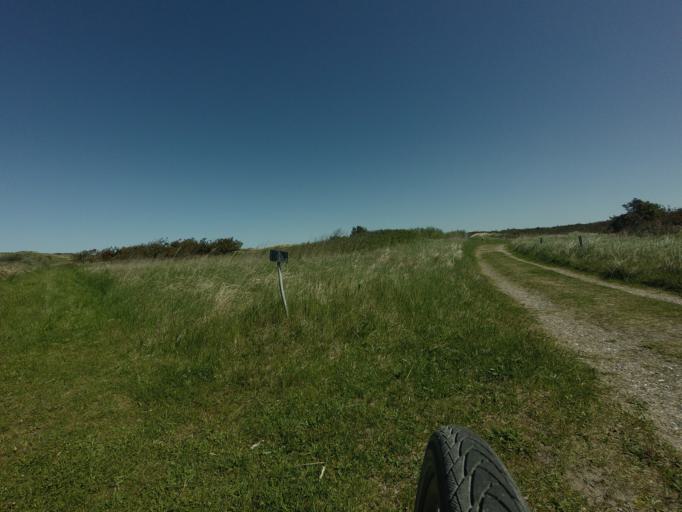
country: DK
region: North Denmark
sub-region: Jammerbugt Kommune
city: Pandrup
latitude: 57.2324
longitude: 9.5582
